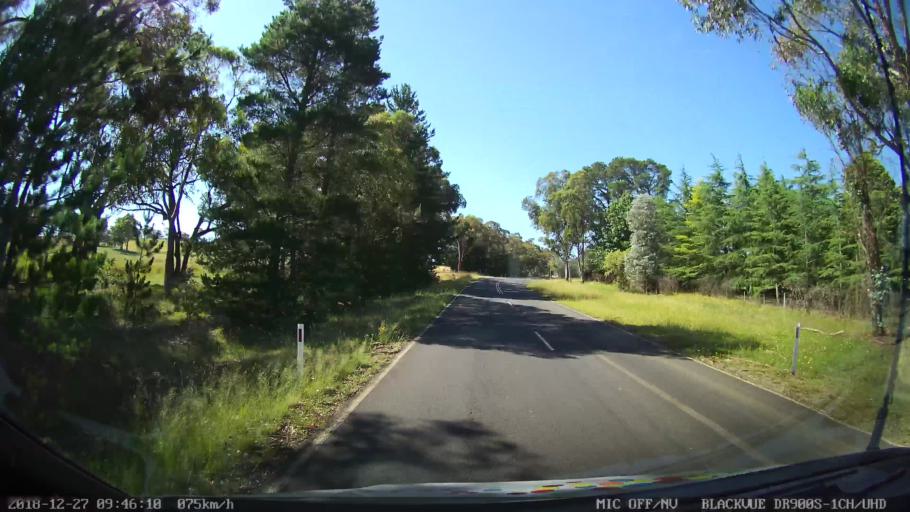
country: AU
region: New South Wales
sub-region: Lithgow
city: Portland
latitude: -33.3328
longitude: 149.9850
